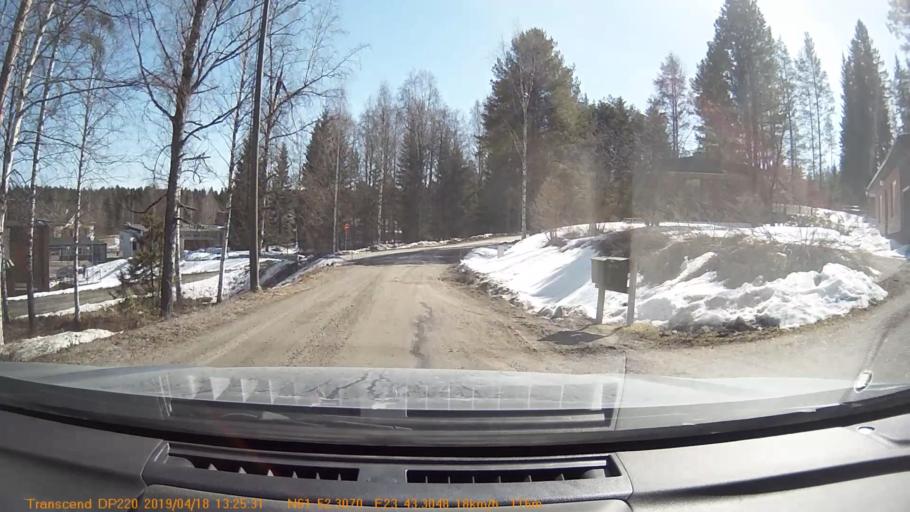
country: FI
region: Pirkanmaa
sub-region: Tampere
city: Kuru
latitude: 61.8718
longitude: 23.7217
